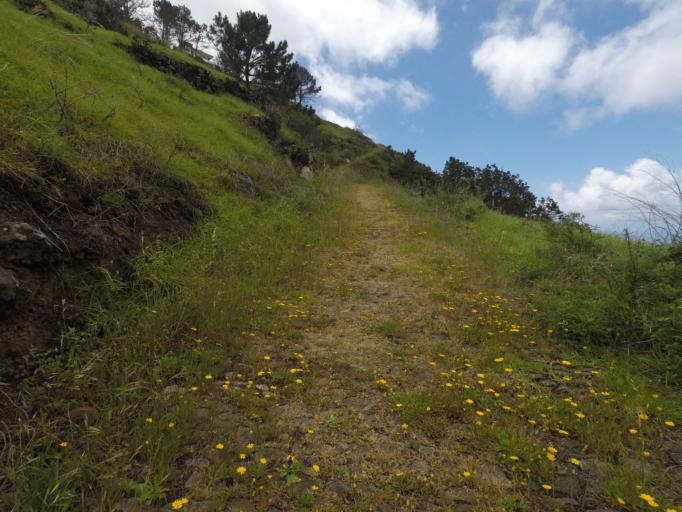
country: PT
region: Madeira
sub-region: Calheta
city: Faja da Ovelha
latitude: 32.7537
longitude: -17.2177
